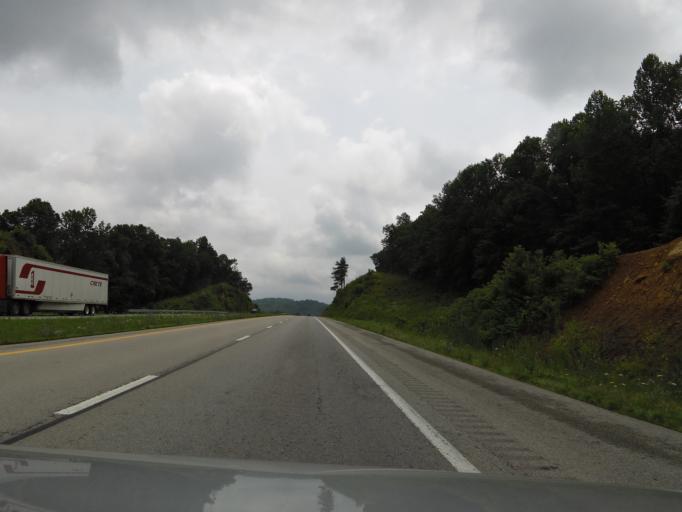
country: US
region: Kentucky
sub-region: Ohio County
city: Oak Grove
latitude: 37.3876
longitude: -86.6869
